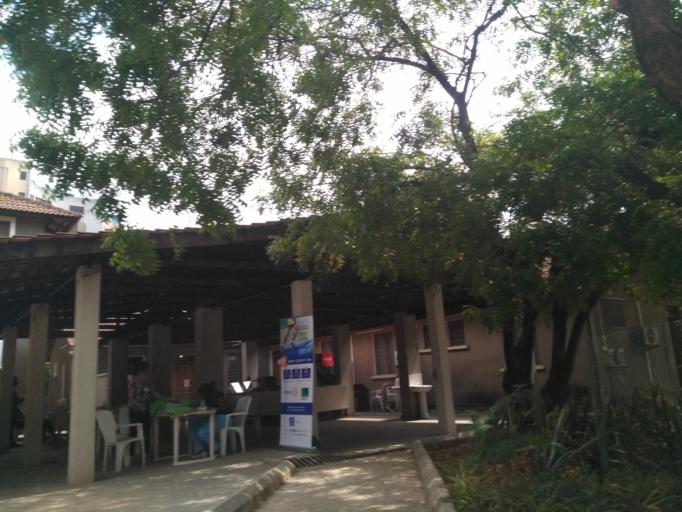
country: TZ
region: Dar es Salaam
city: Magomeni
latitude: -6.7680
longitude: 39.2710
